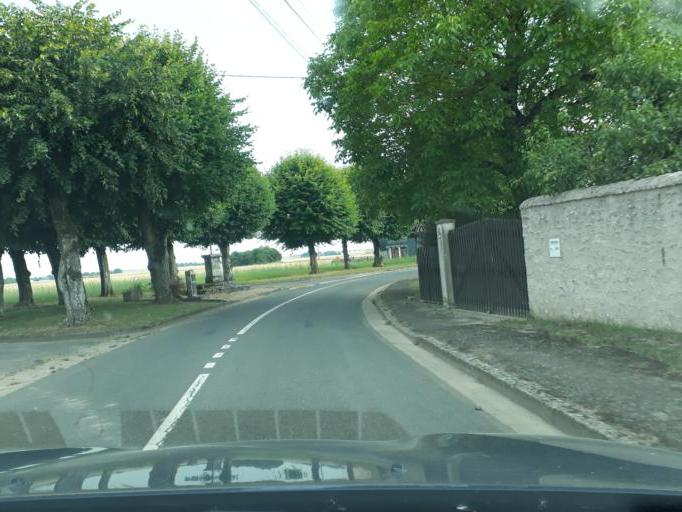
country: FR
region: Centre
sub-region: Departement du Loir-et-Cher
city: Ouzouer-le-Marche
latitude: 47.8158
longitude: 1.4812
